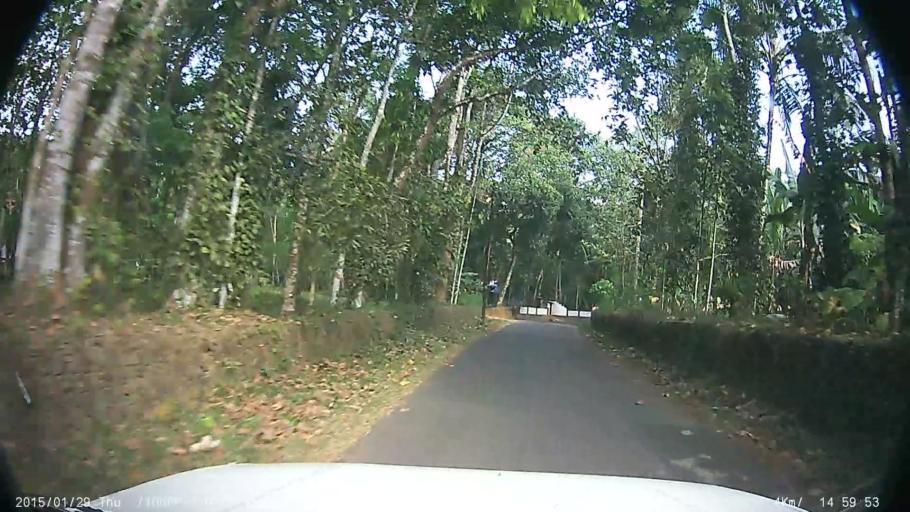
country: IN
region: Kerala
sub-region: Kottayam
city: Palackattumala
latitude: 9.7289
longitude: 76.5633
